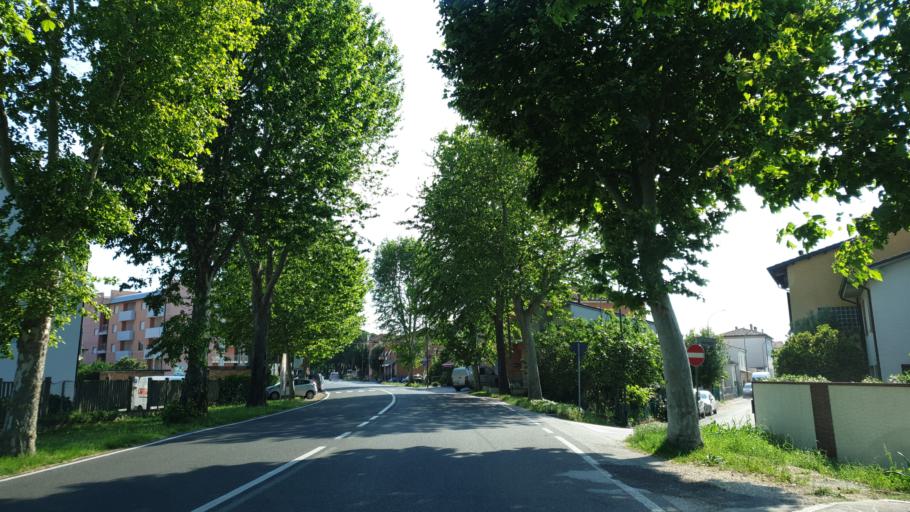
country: IT
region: Emilia-Romagna
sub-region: Provincia di Ravenna
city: Ravenna
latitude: 44.4257
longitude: 12.2131
